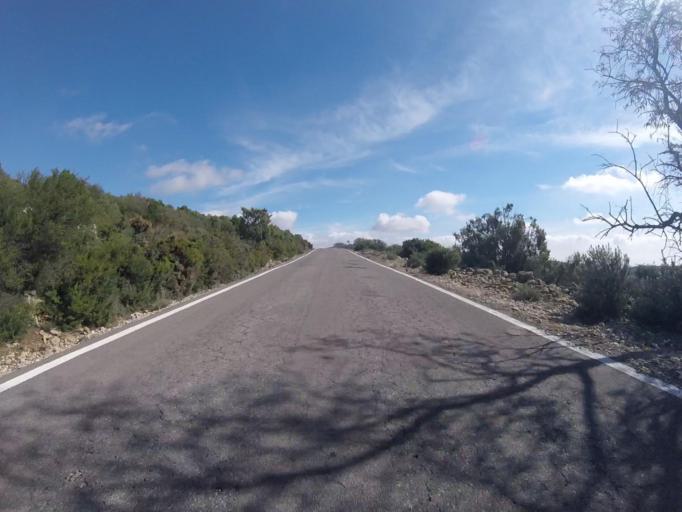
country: ES
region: Valencia
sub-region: Provincia de Castello
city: Sarratella
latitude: 40.3307
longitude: 0.0341
